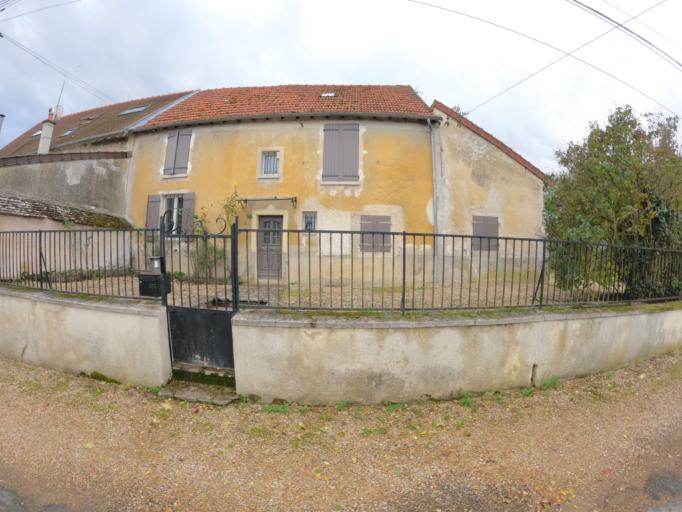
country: FR
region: Ile-de-France
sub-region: Departement de Seine-et-Marne
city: Montry
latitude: 48.8725
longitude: 2.8361
